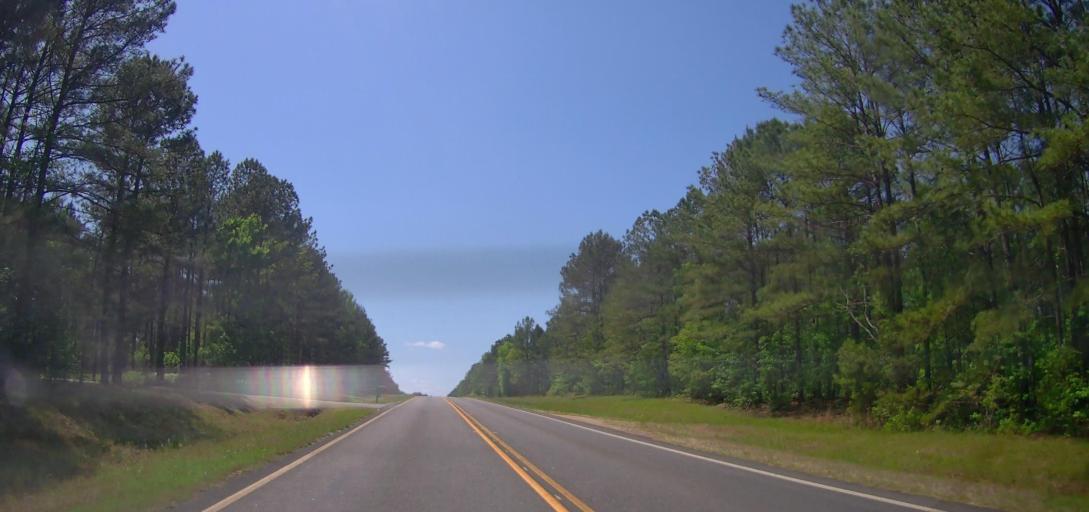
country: US
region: Georgia
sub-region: Putnam County
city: Eatonton
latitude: 33.2015
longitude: -83.4412
